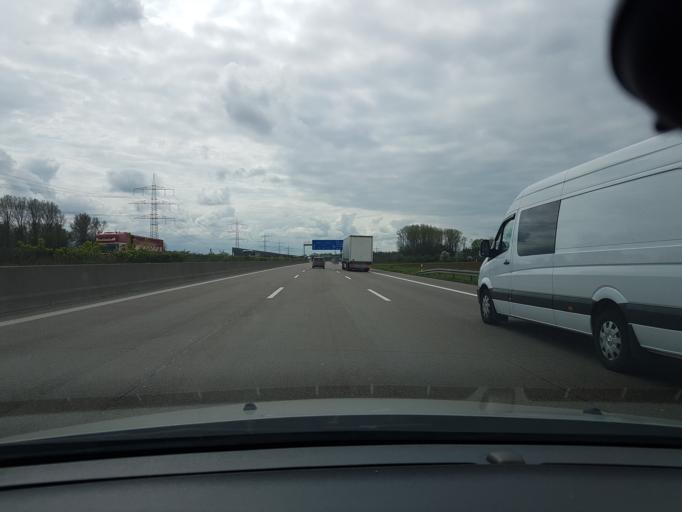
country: DE
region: Baden-Wuerttemberg
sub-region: Karlsruhe Region
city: Ottenhofen
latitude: 48.7323
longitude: 8.1086
